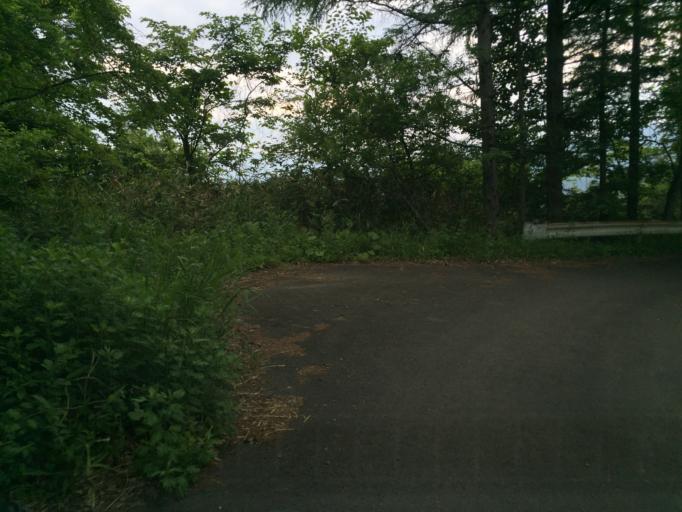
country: JP
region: Fukushima
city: Fukushima-shi
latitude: 37.7199
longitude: 140.3377
